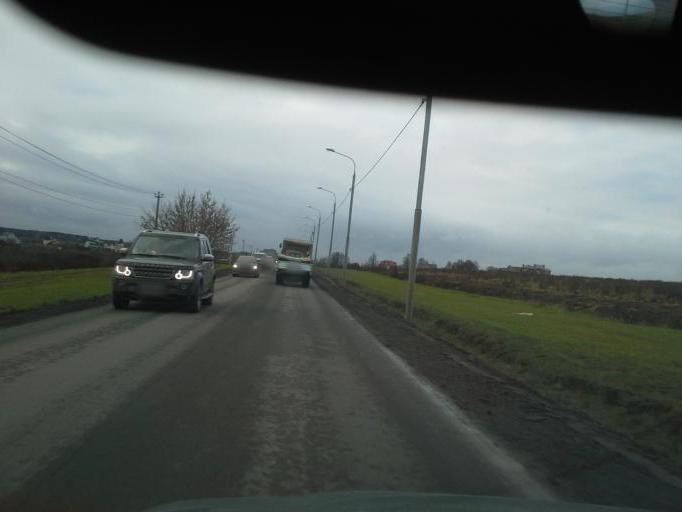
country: RU
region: Moskovskaya
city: Kommunarka
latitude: 55.5576
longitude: 37.4275
